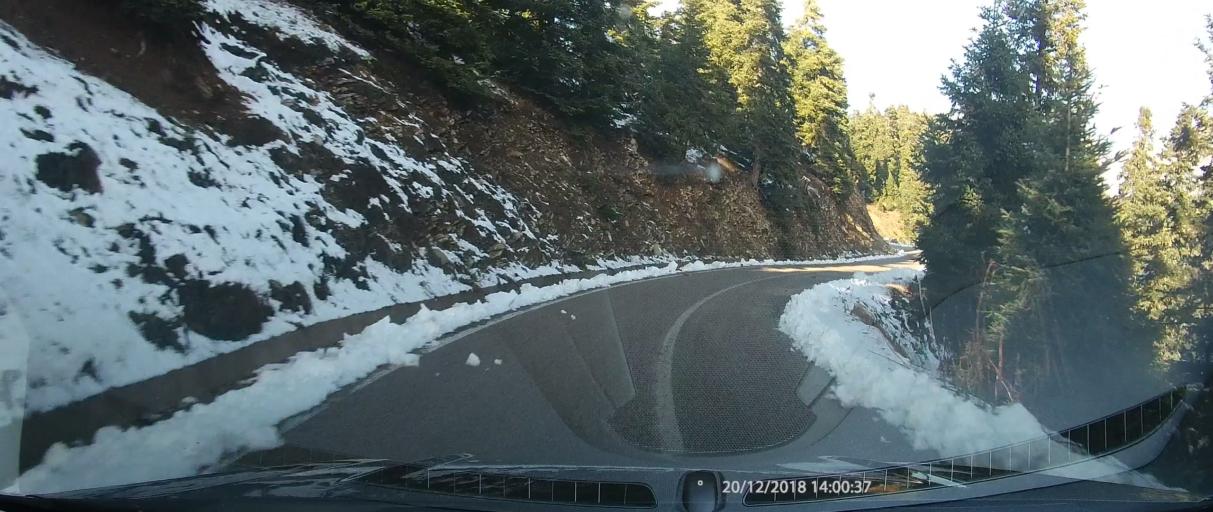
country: GR
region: West Greece
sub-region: Nomos Aitolias kai Akarnanias
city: Thermo
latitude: 38.7260
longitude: 21.6276
